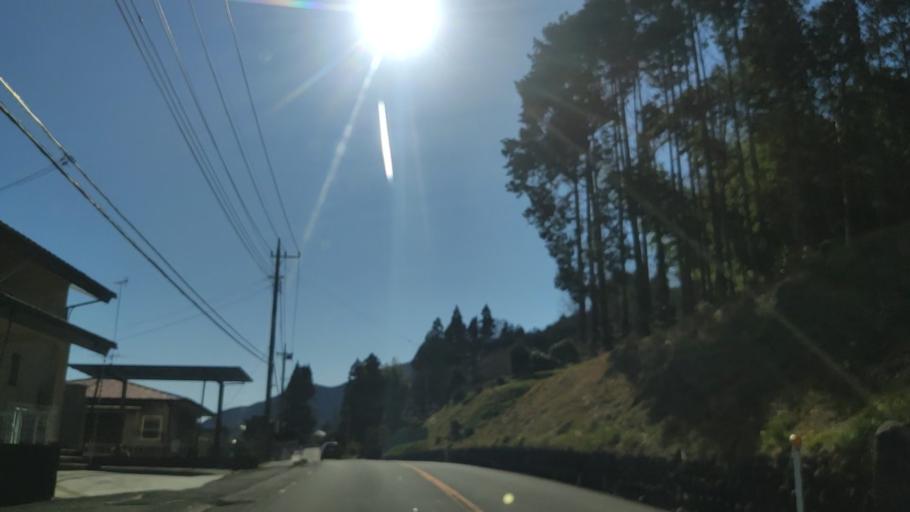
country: JP
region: Shizuoka
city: Fujinomiya
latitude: 35.3116
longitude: 138.5833
